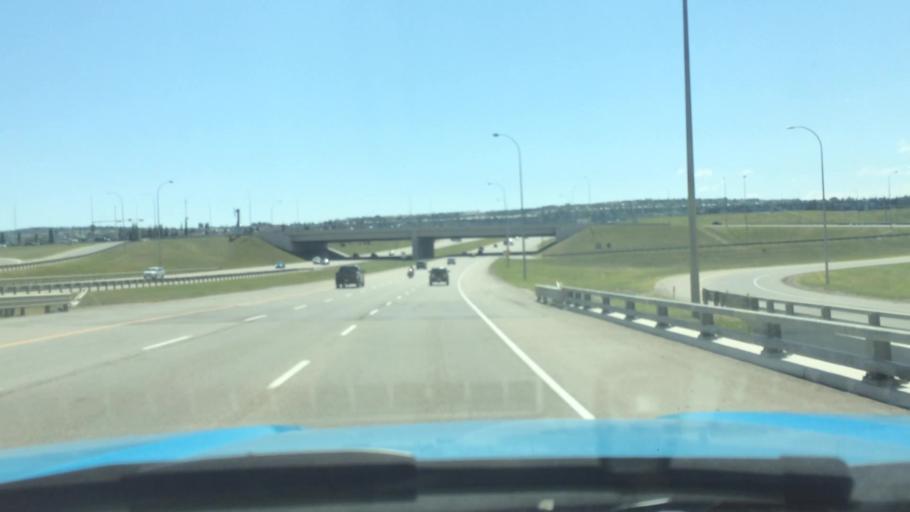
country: CA
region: Alberta
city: Calgary
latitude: 51.1590
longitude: -114.1131
